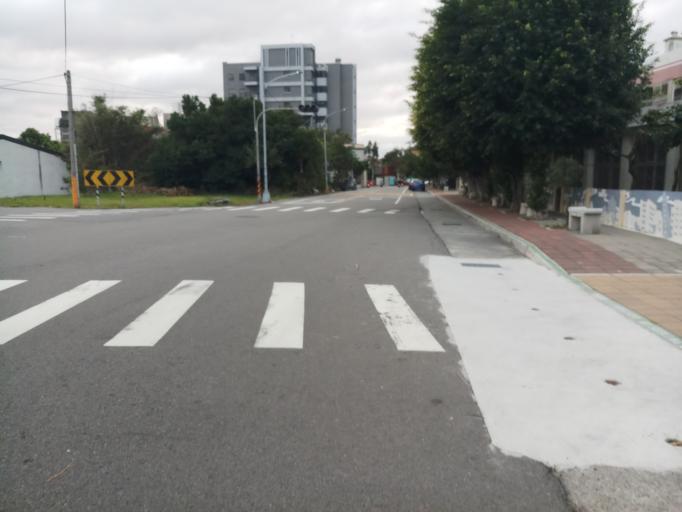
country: TW
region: Taiwan
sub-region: Miaoli
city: Miaoli
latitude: 24.6764
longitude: 120.8626
